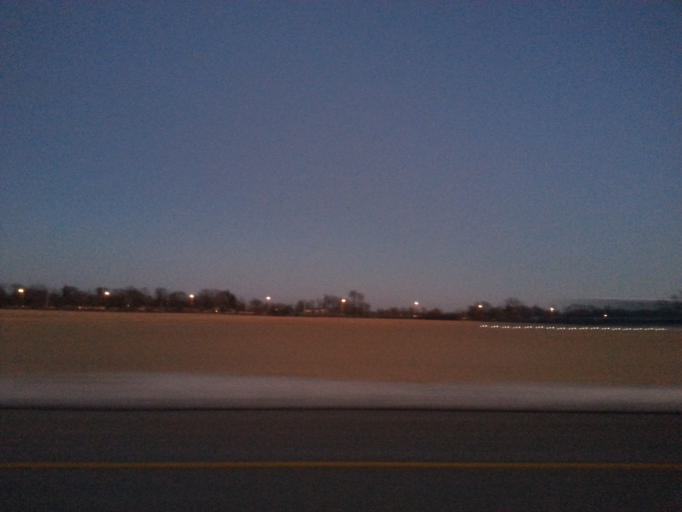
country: US
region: Indiana
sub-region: Lake County
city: Merrillville
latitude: 41.4825
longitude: -87.3220
